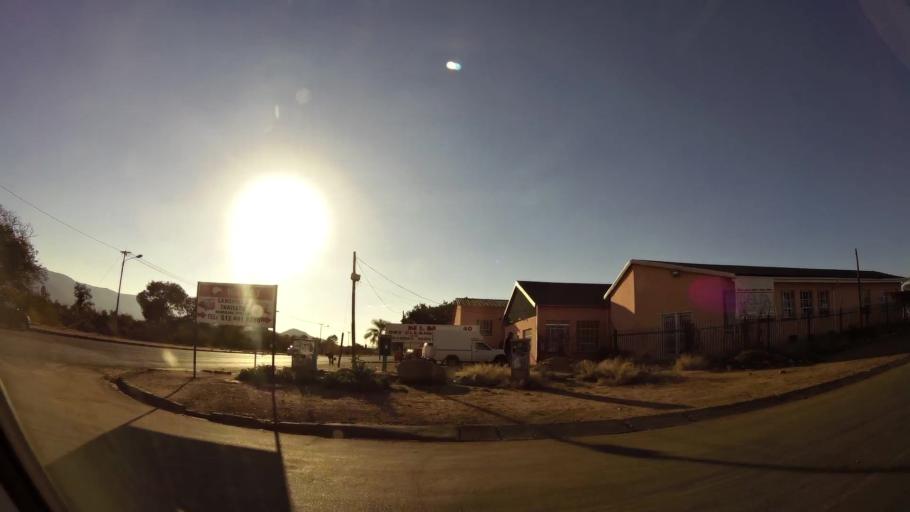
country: ZA
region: Limpopo
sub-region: Waterberg District Municipality
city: Mokopane
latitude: -24.1732
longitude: 29.0008
